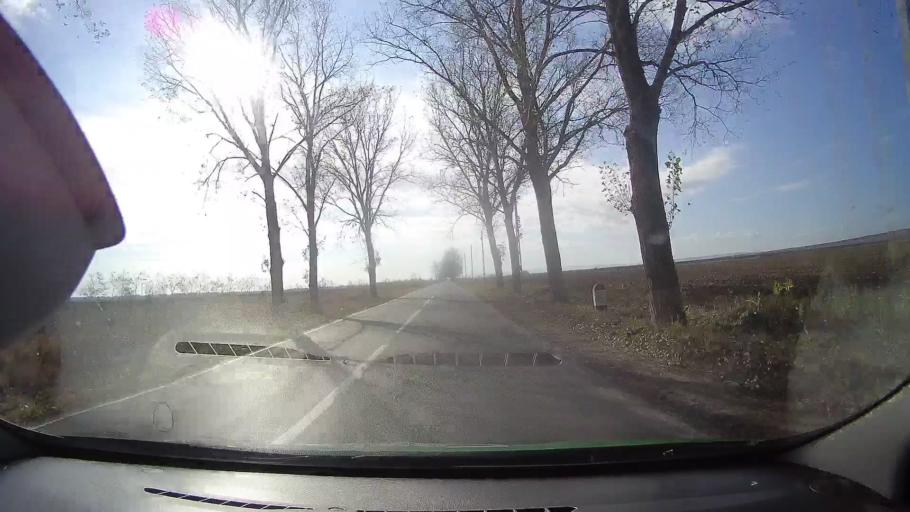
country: RO
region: Tulcea
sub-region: Comuna Valea Nucarilor
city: Agighiol
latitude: 44.9954
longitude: 28.8865
